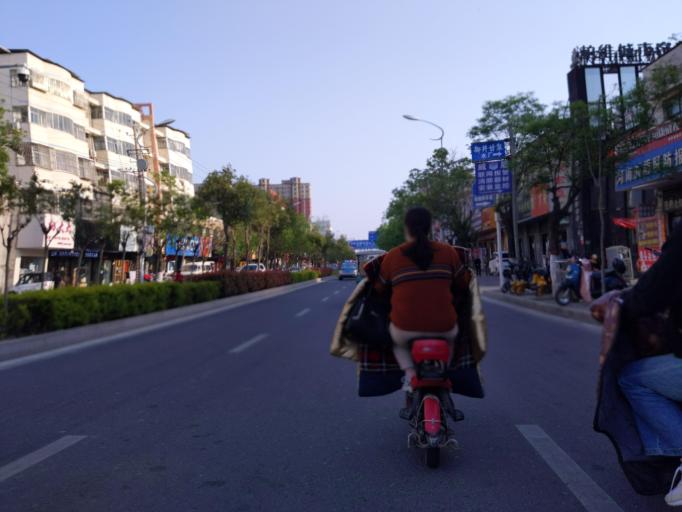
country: CN
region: Henan Sheng
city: Puyang Chengguanzhen
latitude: 35.7010
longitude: 115.0162
